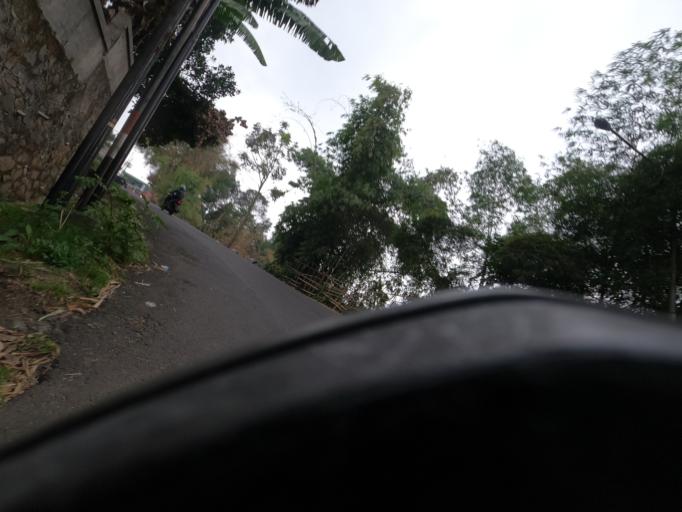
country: ID
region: West Java
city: Lembang
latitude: -6.8186
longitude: 107.6062
